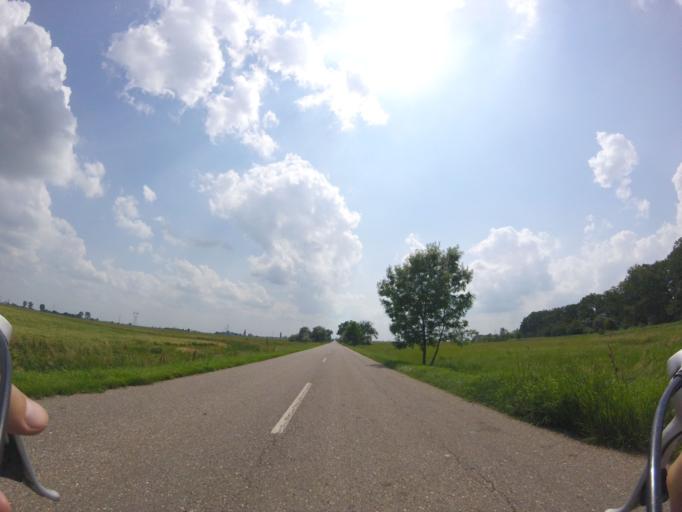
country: HU
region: Heves
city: Kiskore
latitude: 47.5702
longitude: 20.4128
